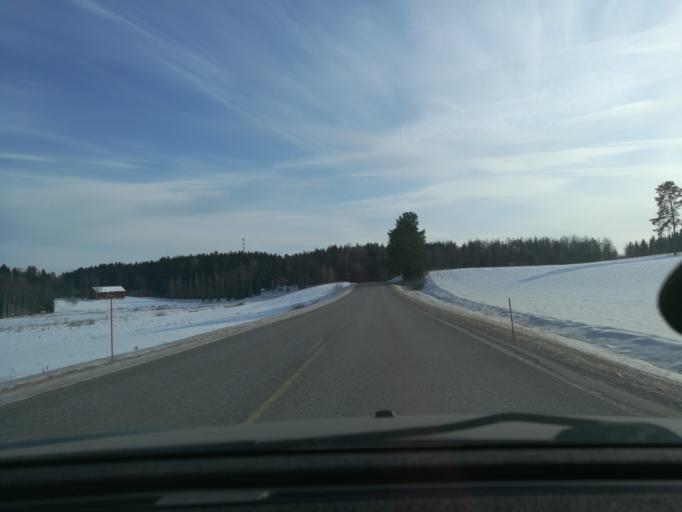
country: FI
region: Uusimaa
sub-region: Helsinki
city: Saukkola
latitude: 60.3919
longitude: 24.0754
